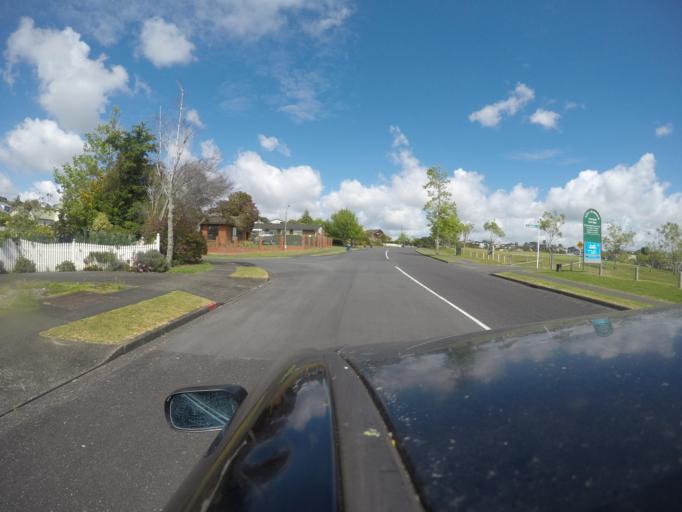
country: NZ
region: Auckland
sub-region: Auckland
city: Rosebank
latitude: -36.8181
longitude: 174.6370
